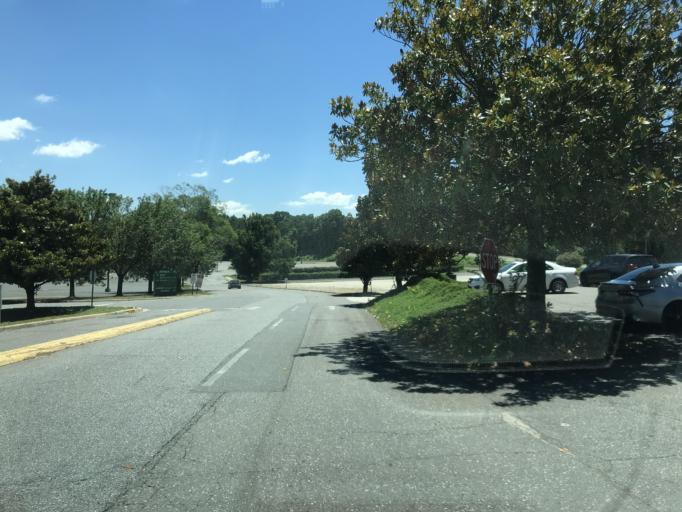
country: US
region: North Carolina
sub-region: Gaston County
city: Ranlo
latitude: 35.2637
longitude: -81.1515
